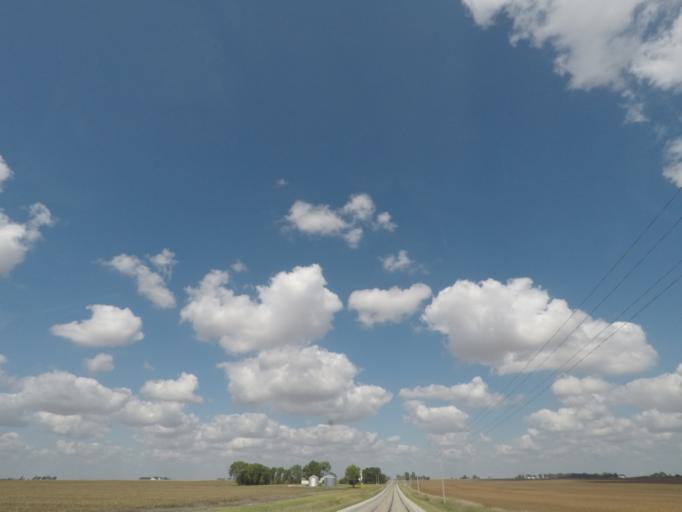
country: US
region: Iowa
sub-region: Story County
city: Nevada
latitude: 42.0500
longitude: -93.4057
